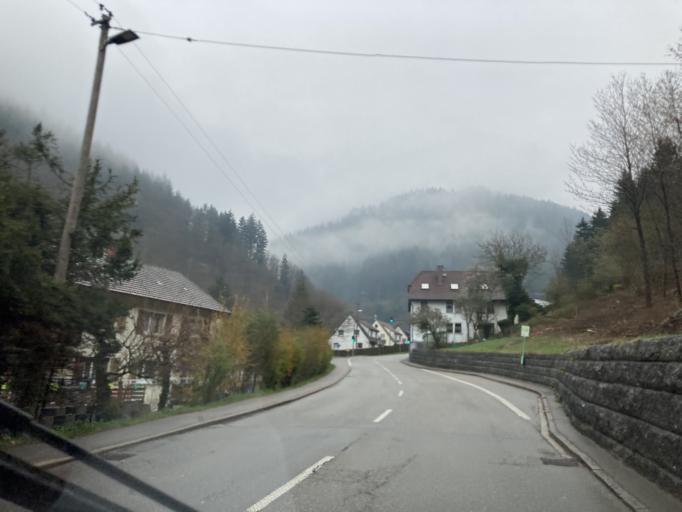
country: DE
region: Baden-Wuerttemberg
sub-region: Freiburg Region
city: Hornberg
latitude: 48.2184
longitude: 8.2449
